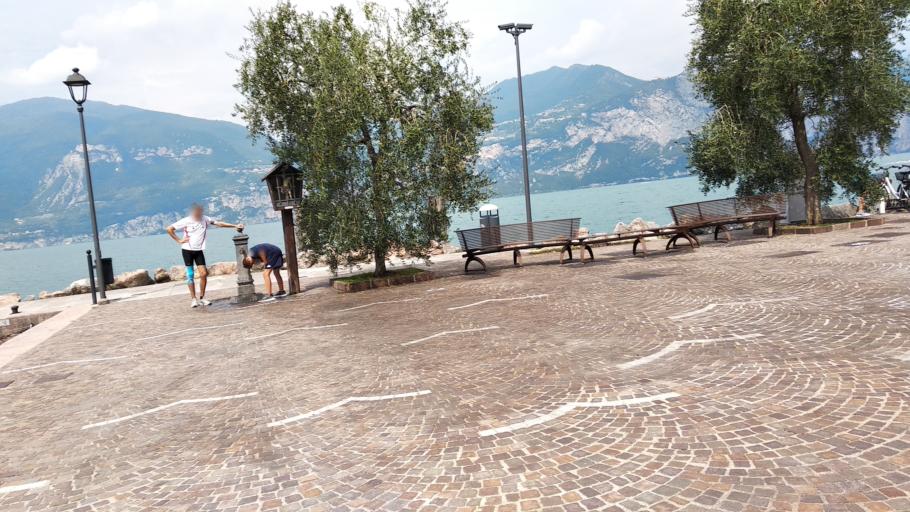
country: IT
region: Veneto
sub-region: Provincia di Verona
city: Magugnano
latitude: 45.7070
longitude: 10.7658
